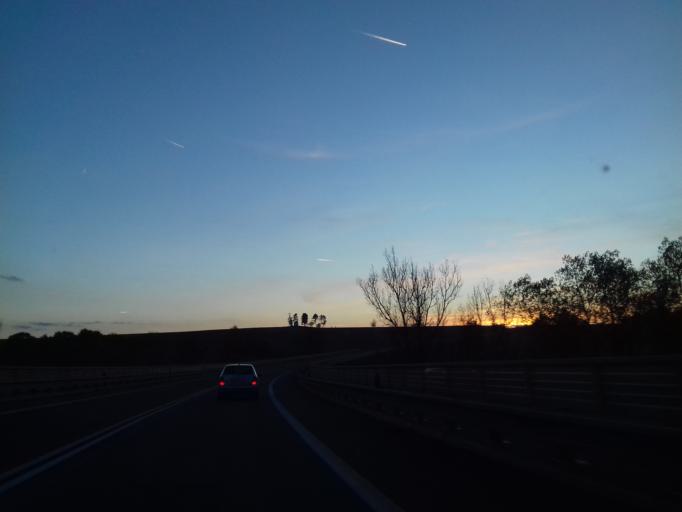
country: CZ
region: Vysocina
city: Pribyslav
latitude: 49.6401
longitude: 15.7012
